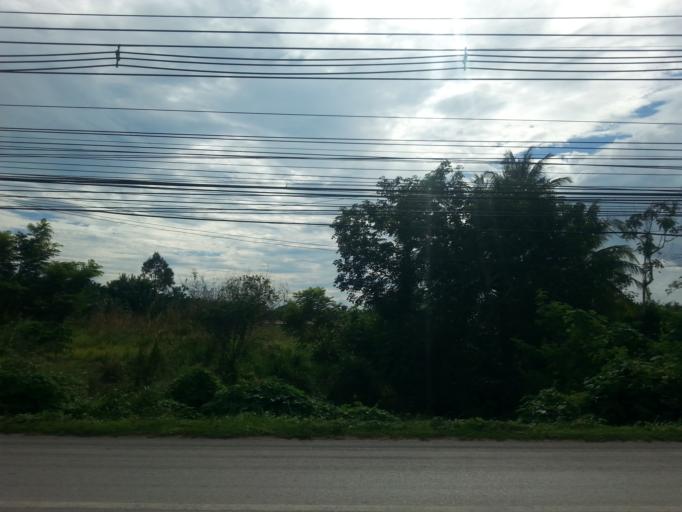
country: TH
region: Krabi
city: Nuea Khlong
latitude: 8.0641
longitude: 99.0046
